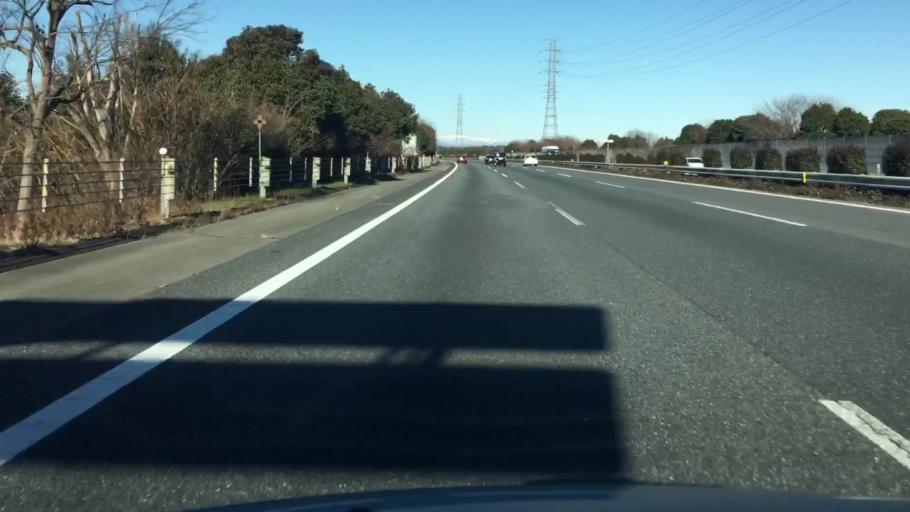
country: JP
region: Saitama
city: Yorii
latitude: 36.1520
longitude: 139.2188
